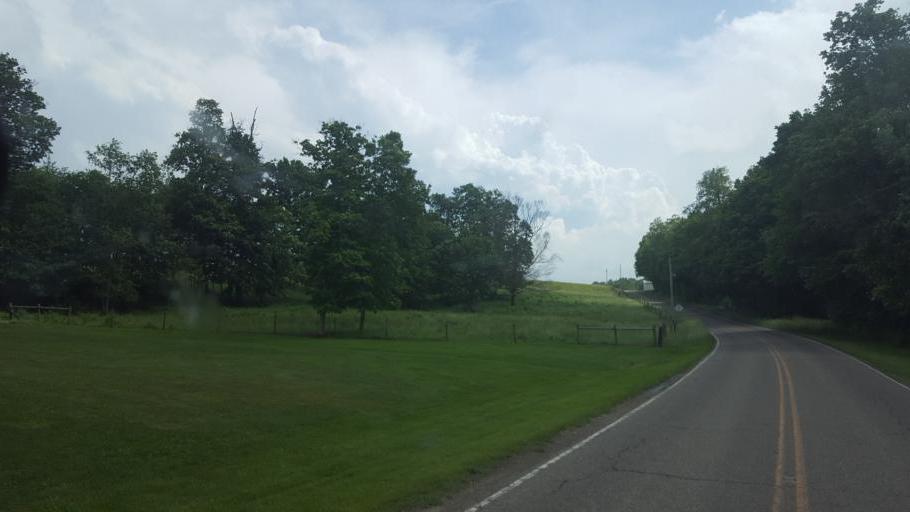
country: US
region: Ohio
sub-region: Knox County
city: Oak Hill
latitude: 40.3104
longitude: -82.1814
